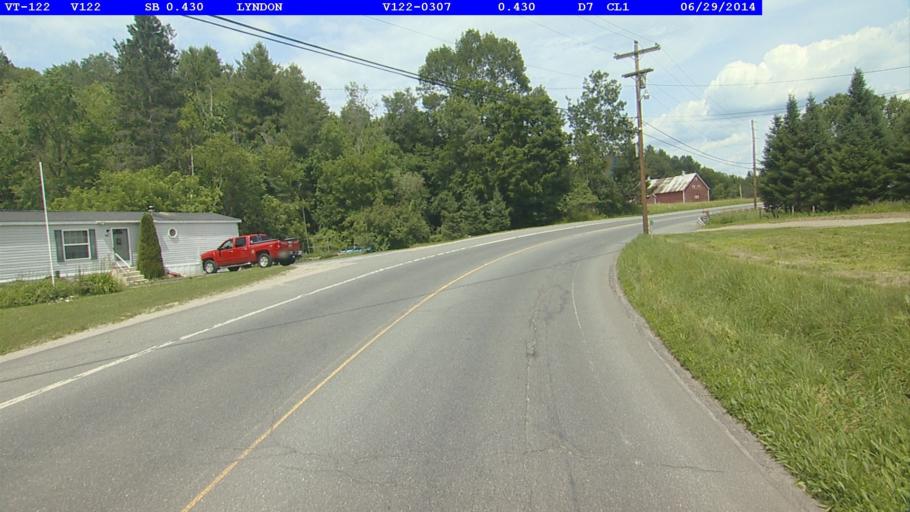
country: US
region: Vermont
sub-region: Caledonia County
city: Lyndonville
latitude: 44.5439
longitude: -72.0082
